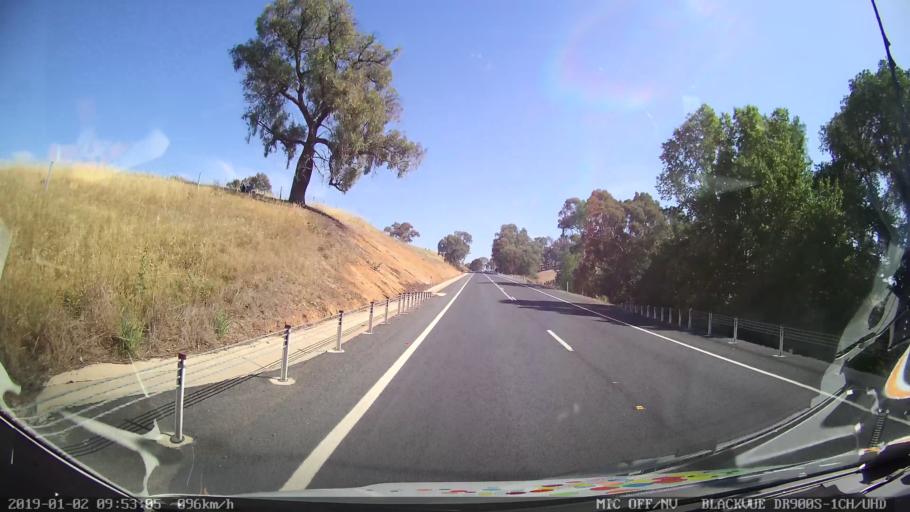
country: AU
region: New South Wales
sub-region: Tumut Shire
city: Tumut
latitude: -35.2523
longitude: 148.2037
